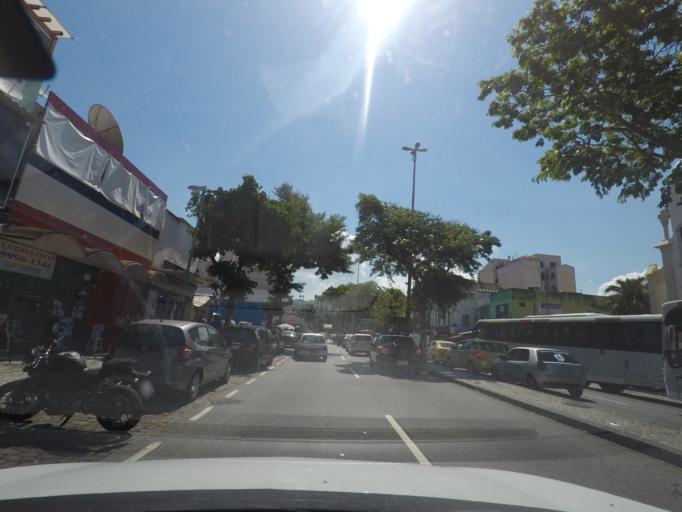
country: BR
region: Rio de Janeiro
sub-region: Rio De Janeiro
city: Rio de Janeiro
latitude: -22.9164
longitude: -43.2491
